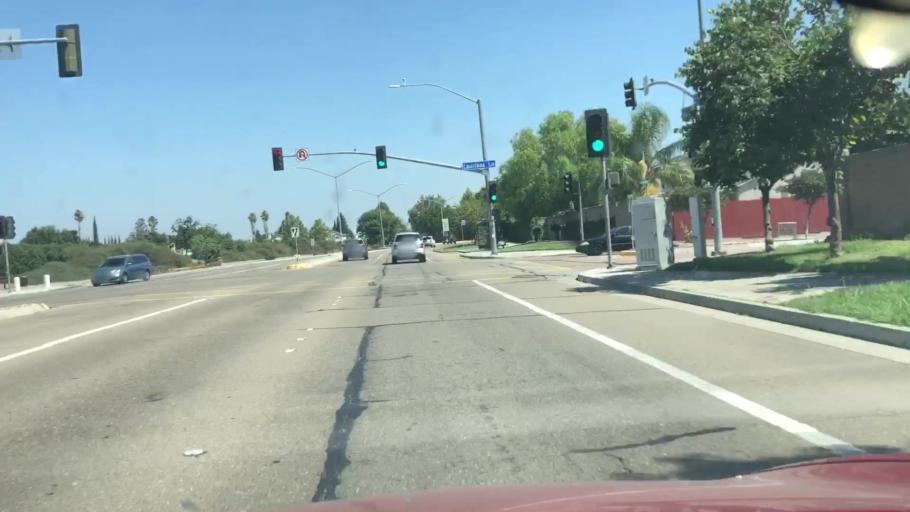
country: US
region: California
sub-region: San Joaquin County
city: Tracy
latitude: 37.7287
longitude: -121.4475
